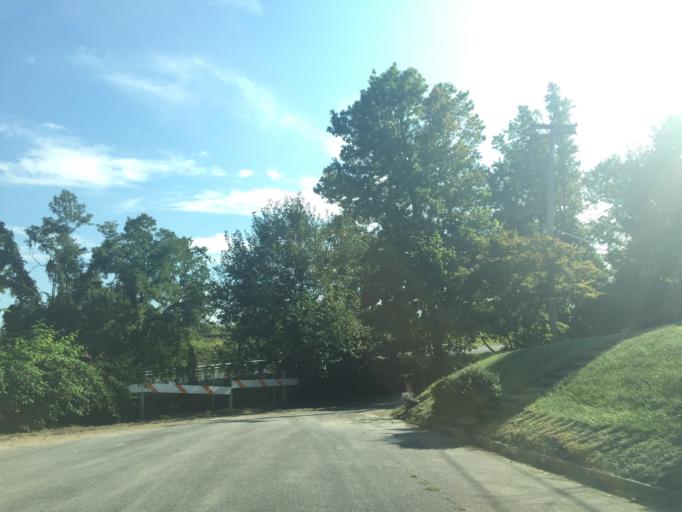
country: US
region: Maryland
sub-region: Carroll County
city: Mount Airy
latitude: 39.3601
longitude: -77.1674
